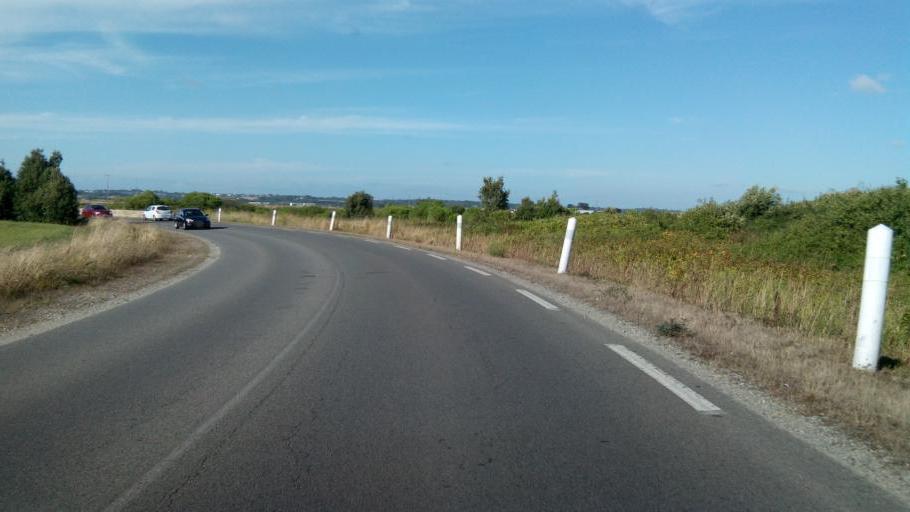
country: FR
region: Pays de la Loire
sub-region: Departement de la Loire-Atlantique
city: Le Pouliguen
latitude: 47.2807
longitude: -2.4530
